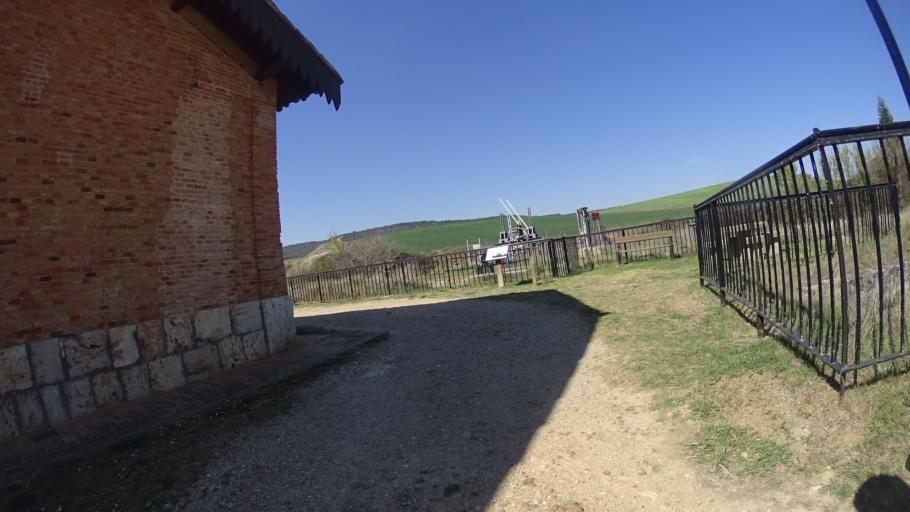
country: ES
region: Castille and Leon
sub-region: Provincia de Palencia
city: Villamuriel de Cerrato
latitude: 41.9219
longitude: -4.5244
